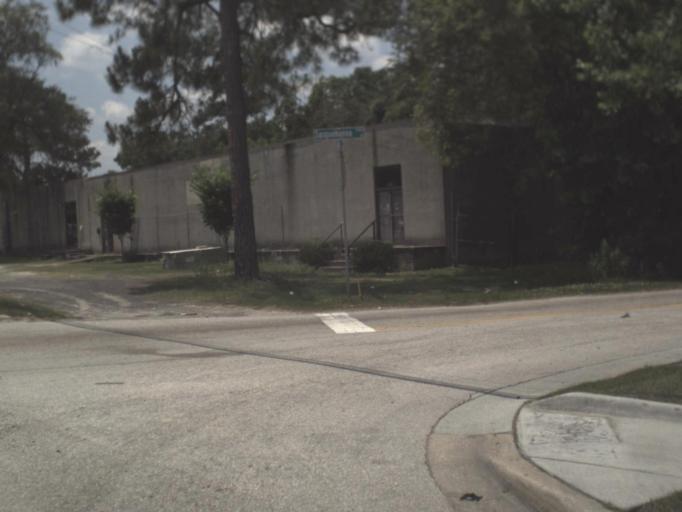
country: US
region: Florida
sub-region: Duval County
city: Jacksonville
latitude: 30.3613
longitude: -81.7313
